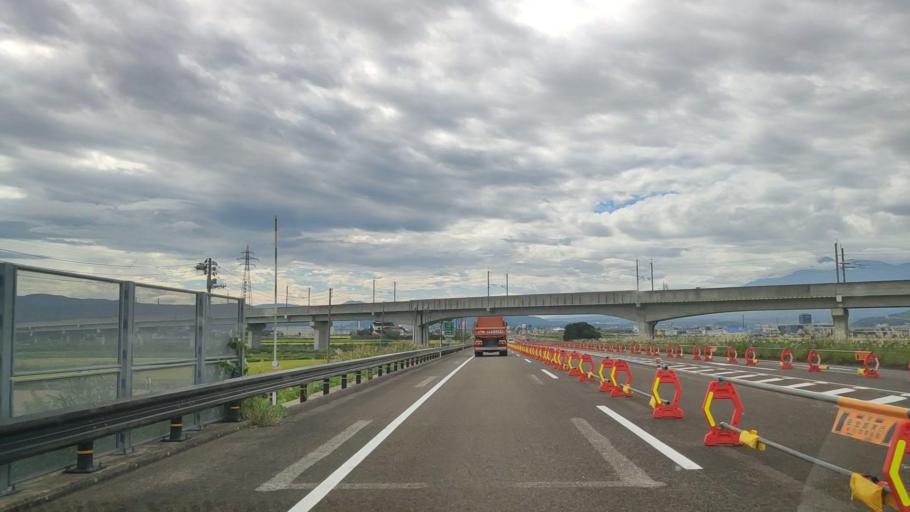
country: JP
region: Niigata
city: Arai
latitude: 37.0694
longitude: 138.2640
